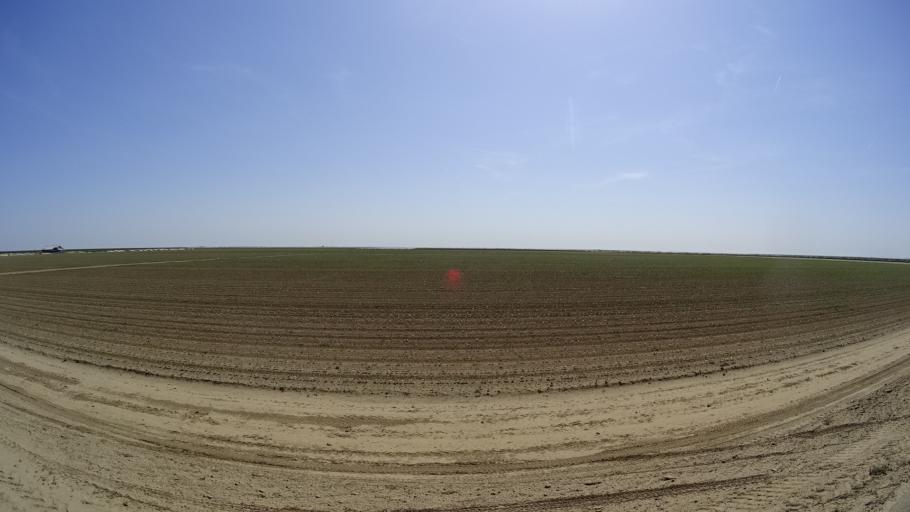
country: US
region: California
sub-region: Kings County
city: Kettleman City
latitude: 36.0712
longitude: -120.0036
